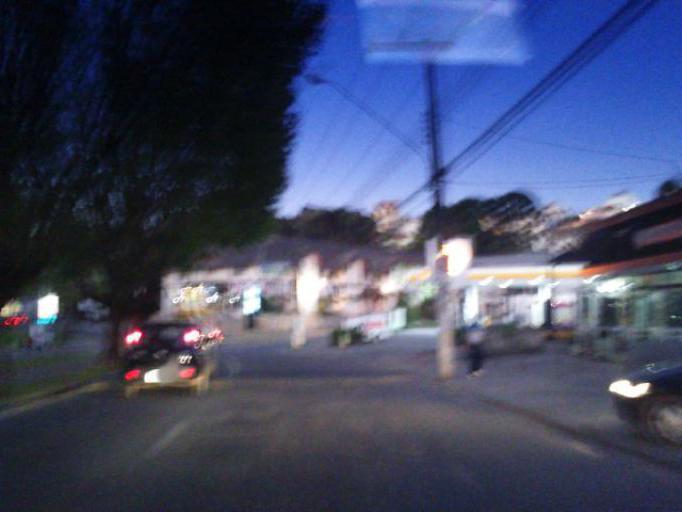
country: BR
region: Sao Paulo
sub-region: Campos Do Jordao
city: Campos do Jordao
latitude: -22.7338
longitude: -45.5854
